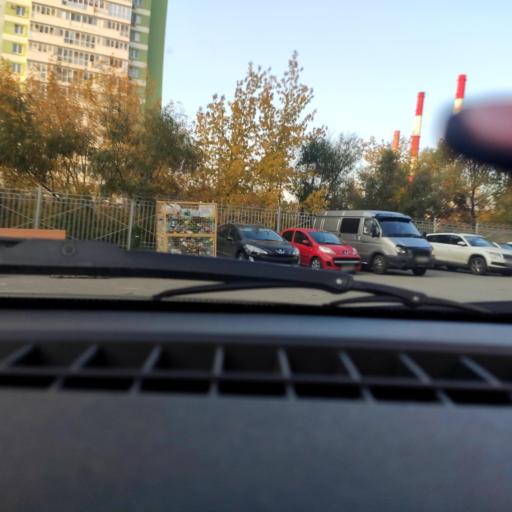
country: RU
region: Bashkortostan
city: Ufa
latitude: 54.7850
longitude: 56.1131
